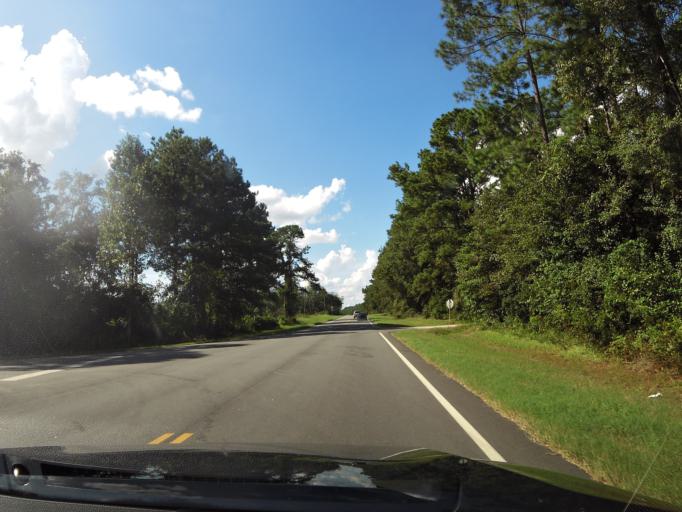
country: US
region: Georgia
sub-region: Echols County
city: Statenville
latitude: 30.7588
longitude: -83.1205
